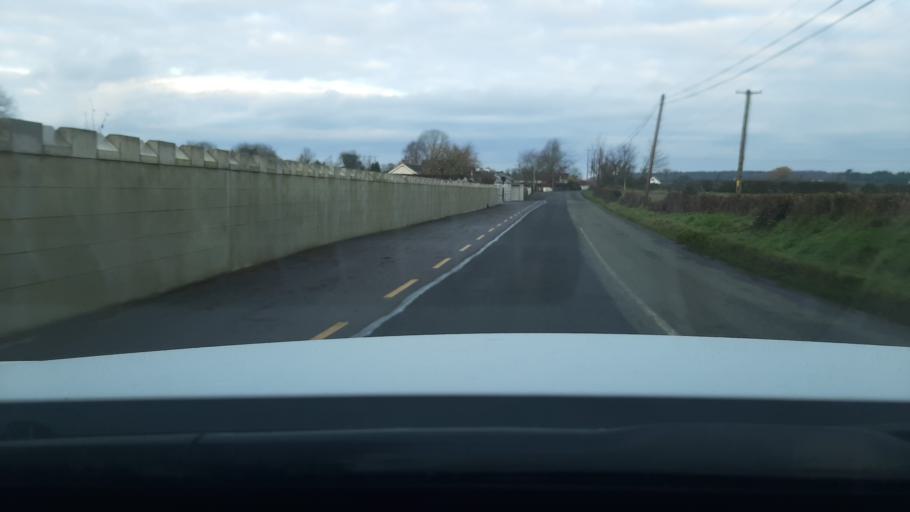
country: IE
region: Leinster
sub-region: Kildare
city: Rathangan
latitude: 53.2275
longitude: -7.0067
